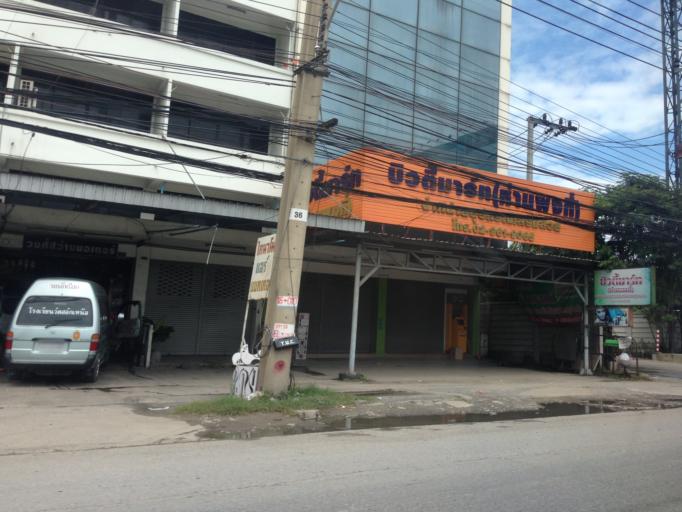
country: TH
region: Nonthaburi
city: Pak Kret
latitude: 13.9345
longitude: 100.5360
